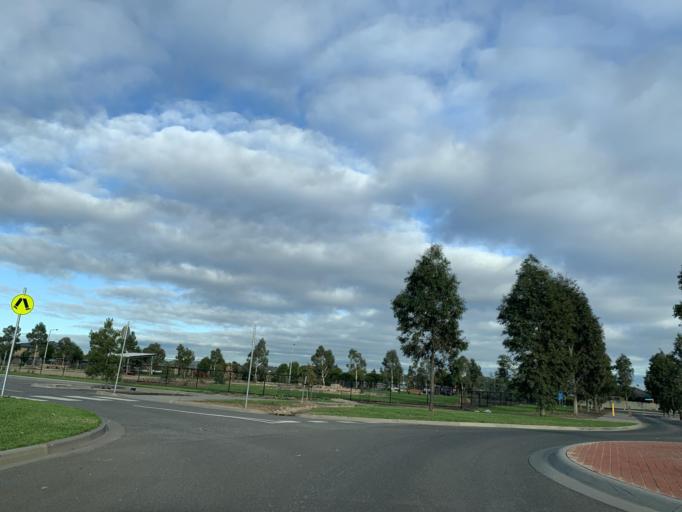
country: AU
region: Victoria
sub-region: Casey
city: Cranbourne East
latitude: -38.1227
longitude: 145.3077
